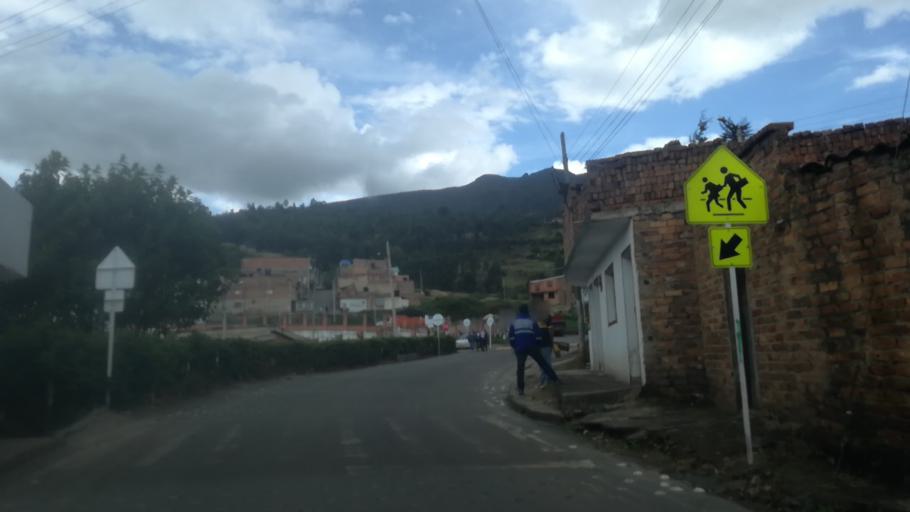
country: CO
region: Boyaca
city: Socha Viejo
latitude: 5.9965
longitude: -72.6900
